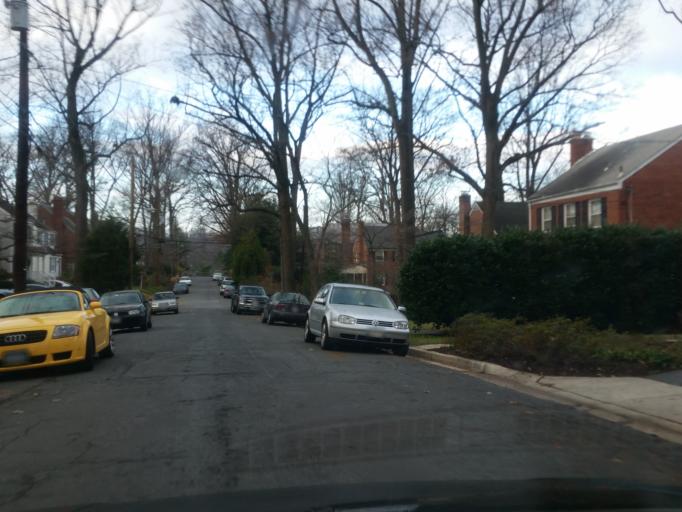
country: US
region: Maryland
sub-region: Montgomery County
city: Forest Glen
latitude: 38.9910
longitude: -77.0565
